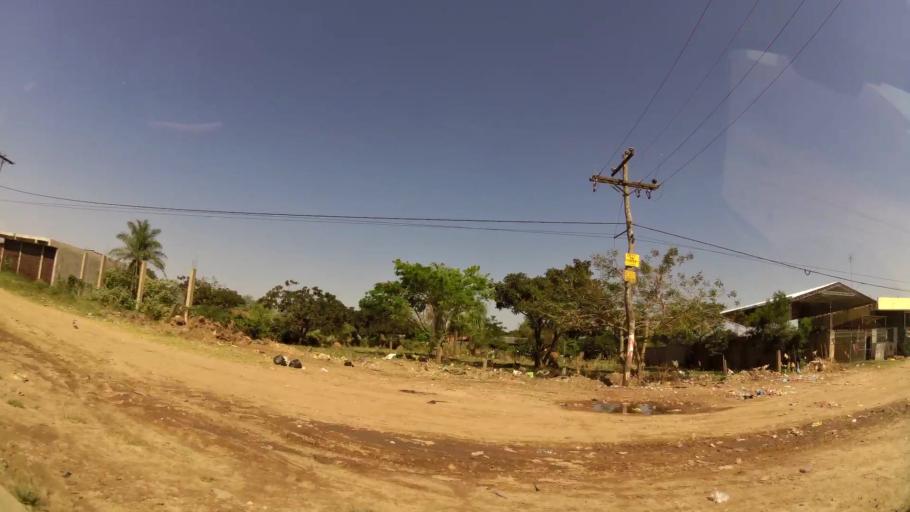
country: BO
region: Santa Cruz
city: Cotoca
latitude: -17.7302
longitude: -63.0930
